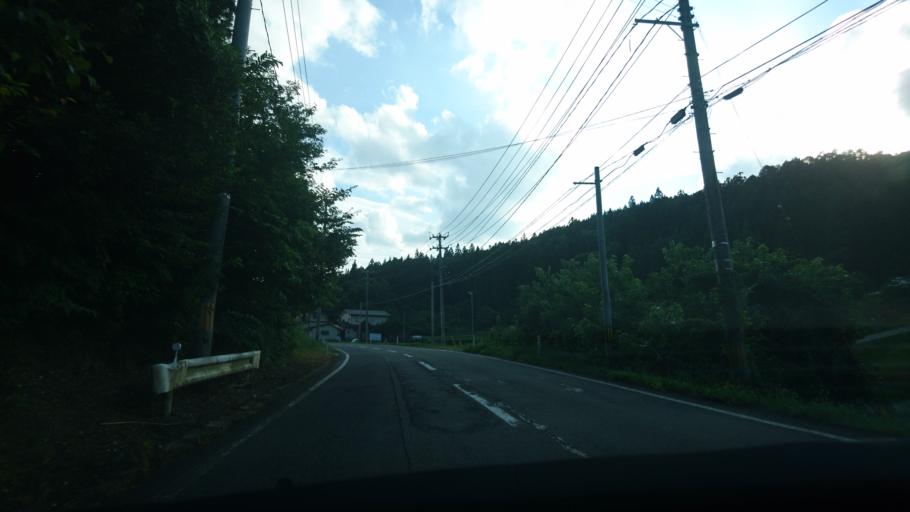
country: JP
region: Iwate
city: Ichinoseki
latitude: 39.0134
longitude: 141.2881
